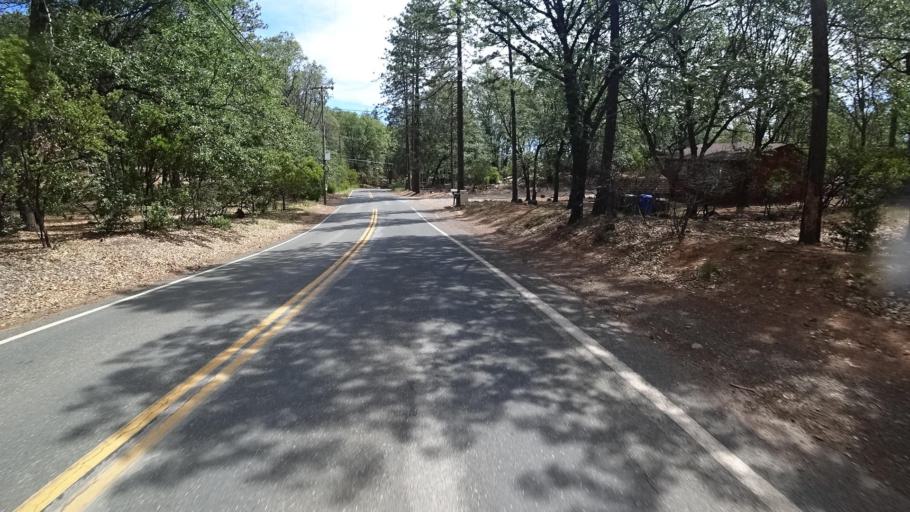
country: US
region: California
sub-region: Lake County
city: Cobb
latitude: 38.8645
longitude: -122.6940
